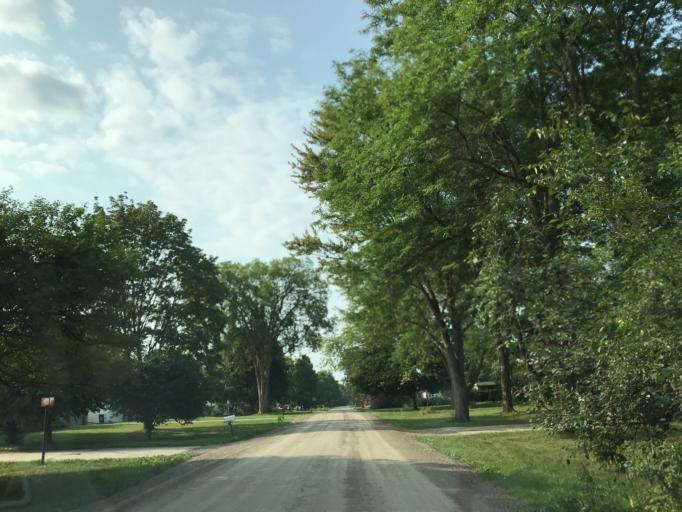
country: US
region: Michigan
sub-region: Washtenaw County
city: Ypsilanti
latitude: 42.2506
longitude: -83.6794
